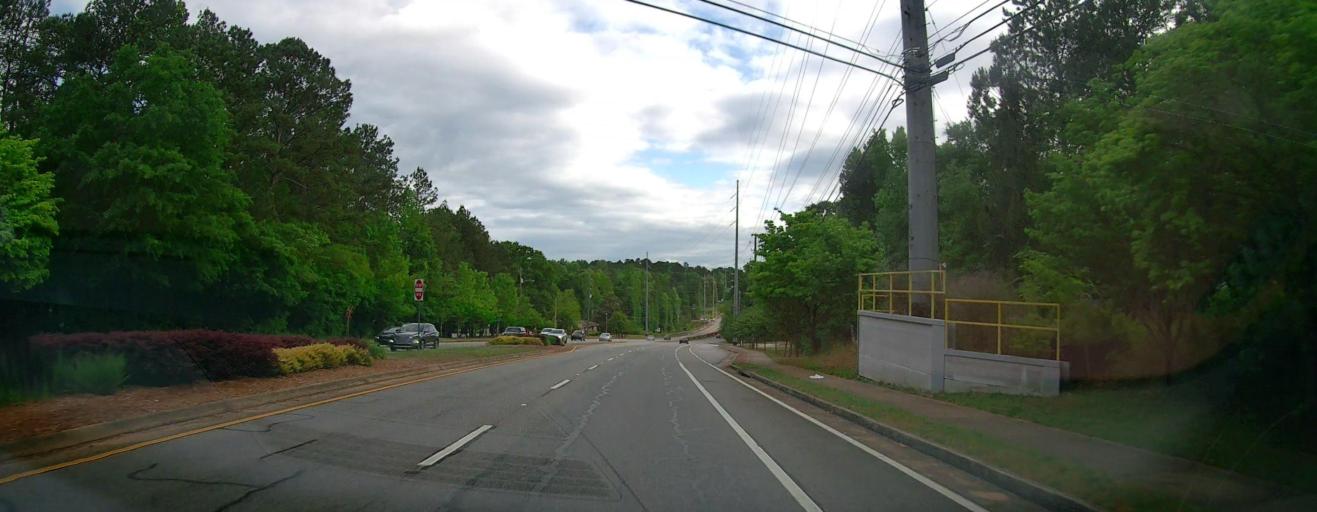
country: US
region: Georgia
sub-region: Clarke County
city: Country Club Estates
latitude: 33.9271
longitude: -83.4388
